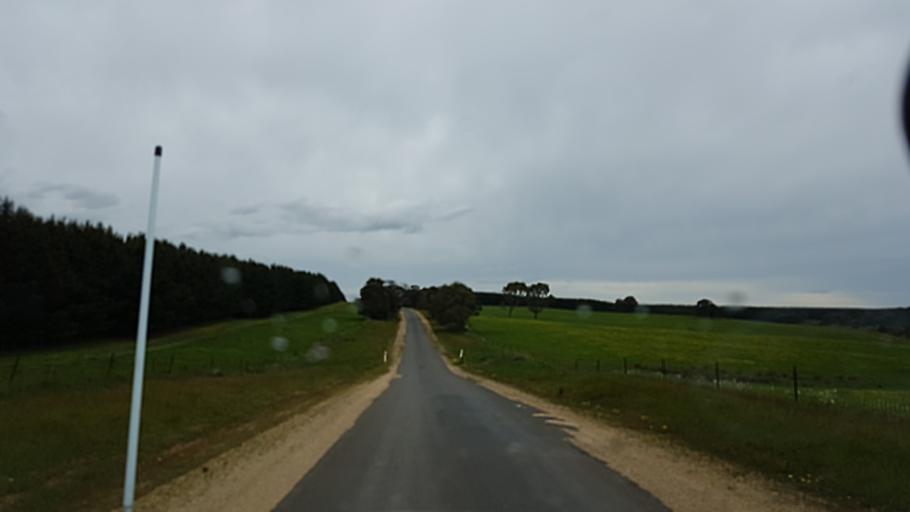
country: AU
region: Victoria
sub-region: Moorabool
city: Bacchus Marsh
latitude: -37.7834
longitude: 144.1452
